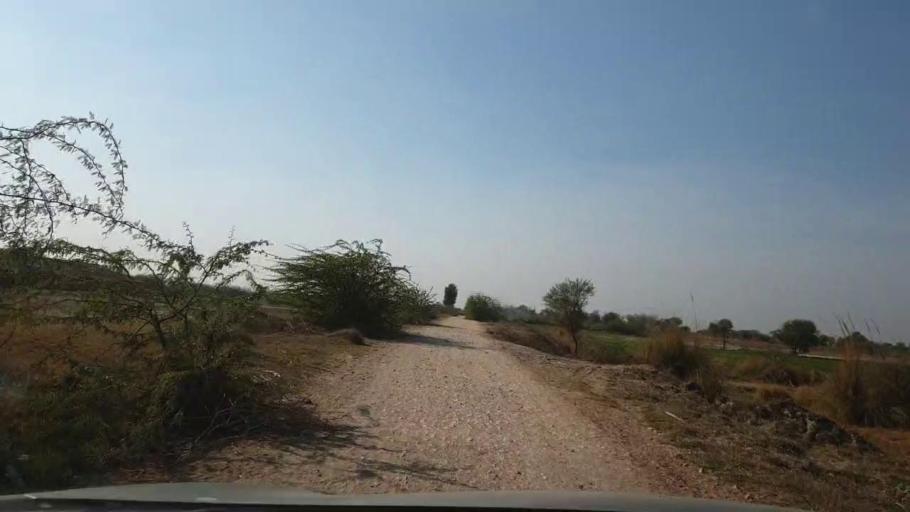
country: PK
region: Sindh
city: Berani
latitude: 25.7201
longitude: 68.7658
